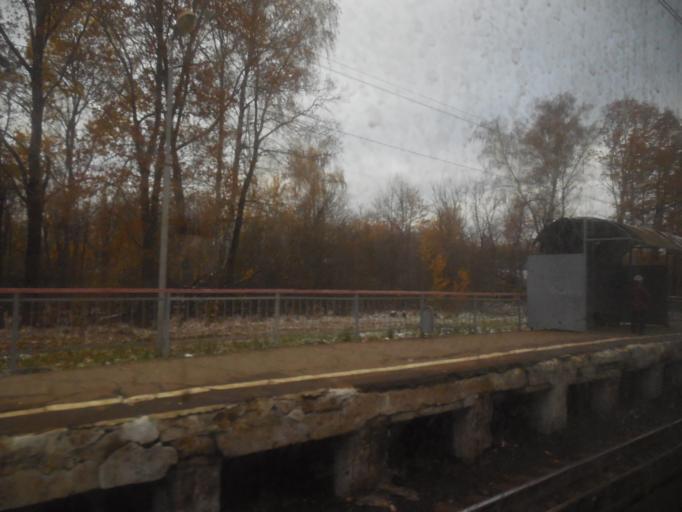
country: RU
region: Moskovskaya
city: Novoivanovskoye
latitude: 55.6975
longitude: 37.3388
